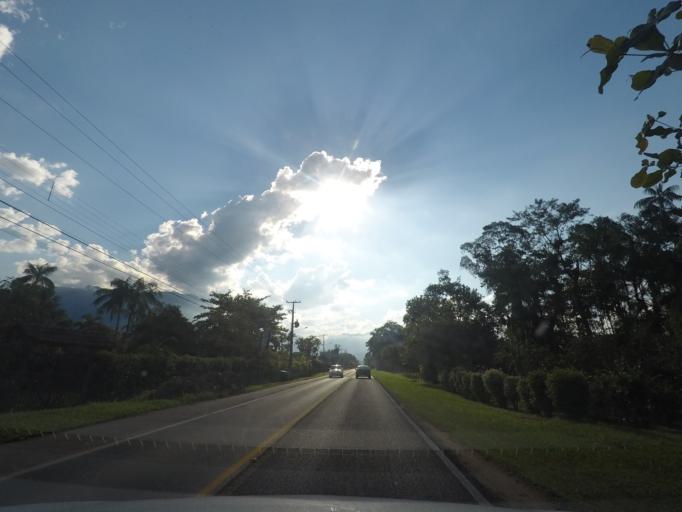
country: BR
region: Parana
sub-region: Antonina
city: Antonina
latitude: -25.4685
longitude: -48.8447
